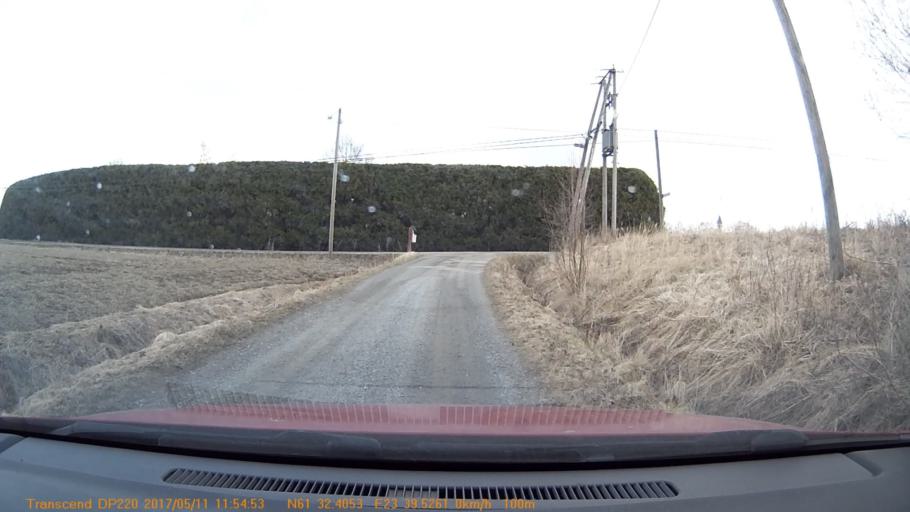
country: FI
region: Pirkanmaa
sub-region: Tampere
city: Yloejaervi
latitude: 61.5401
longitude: 23.6588
